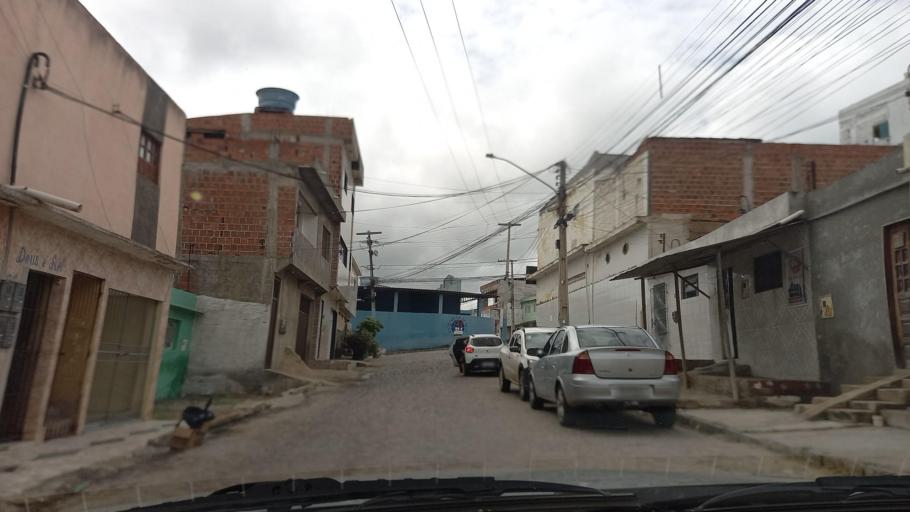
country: BR
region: Pernambuco
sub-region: Caruaru
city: Caruaru
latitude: -8.2718
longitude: -35.9550
